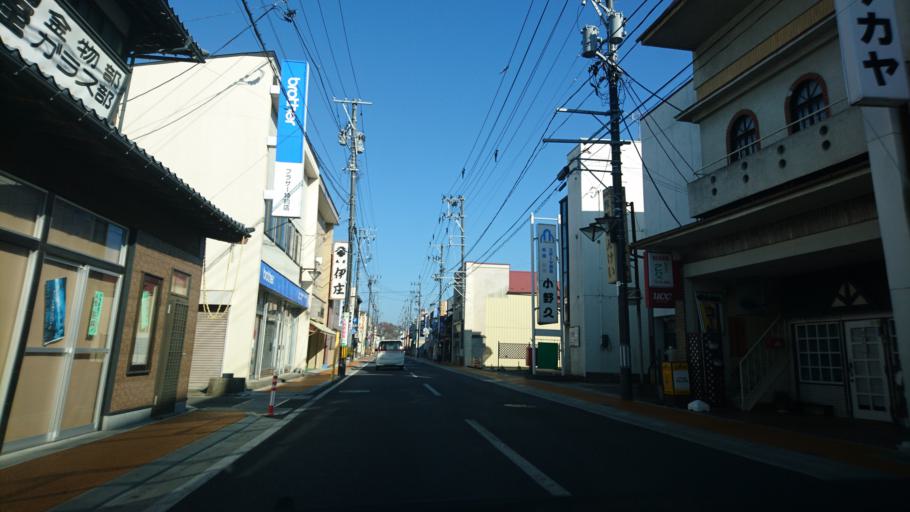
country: JP
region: Iwate
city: Ichinoseki
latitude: 38.9188
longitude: 141.3340
